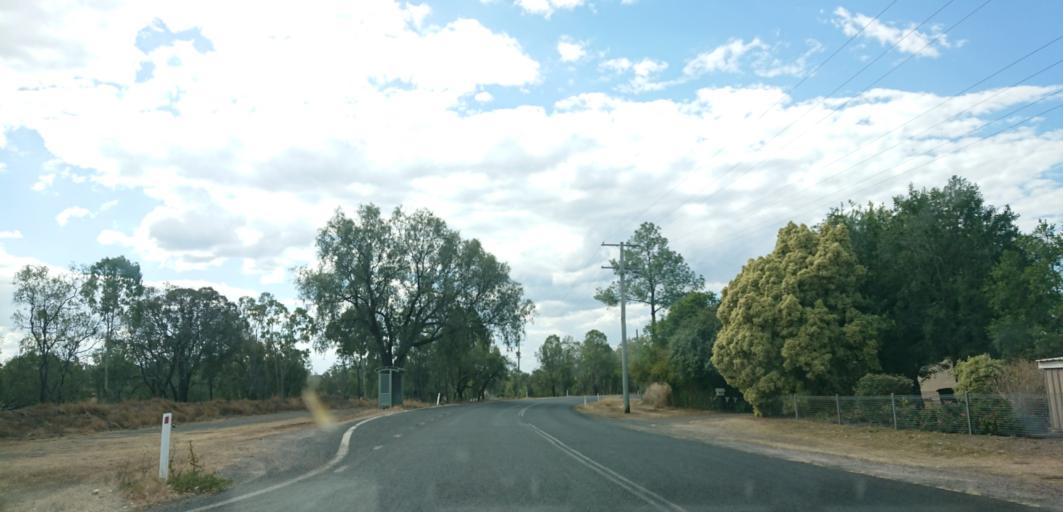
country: AU
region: Queensland
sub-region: Lockyer Valley
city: Gatton
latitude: -27.6084
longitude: 152.2094
